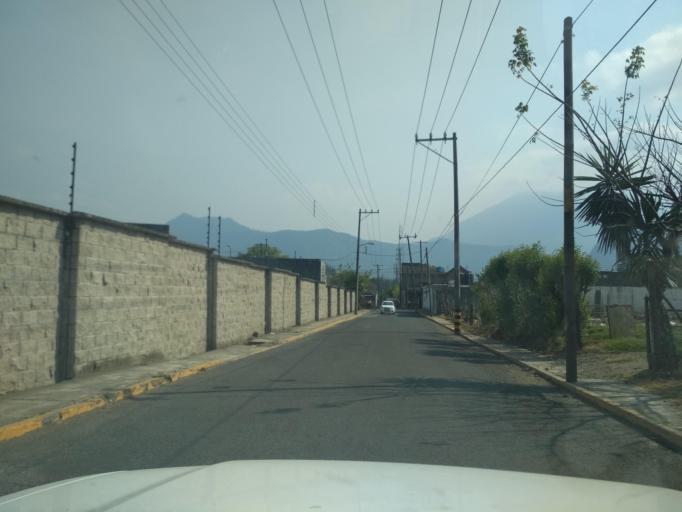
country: MX
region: Veracruz
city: Jalapilla
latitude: 18.8370
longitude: -97.0856
